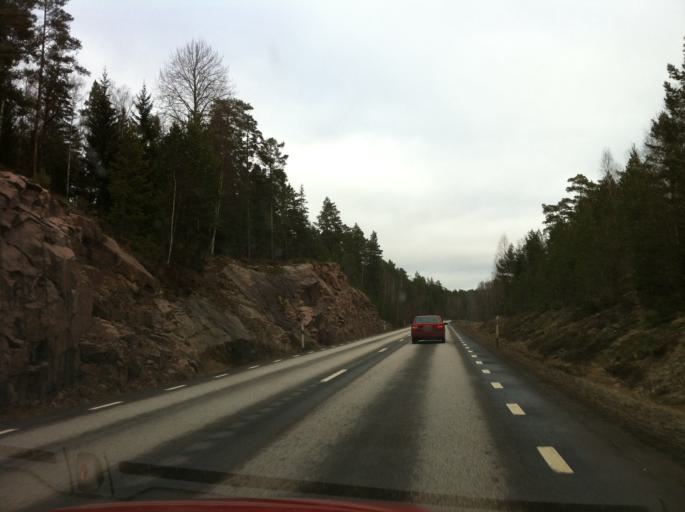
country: SE
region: Kalmar
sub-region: Vimmerby Kommun
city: Vimmerby
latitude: 57.6350
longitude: 15.7534
